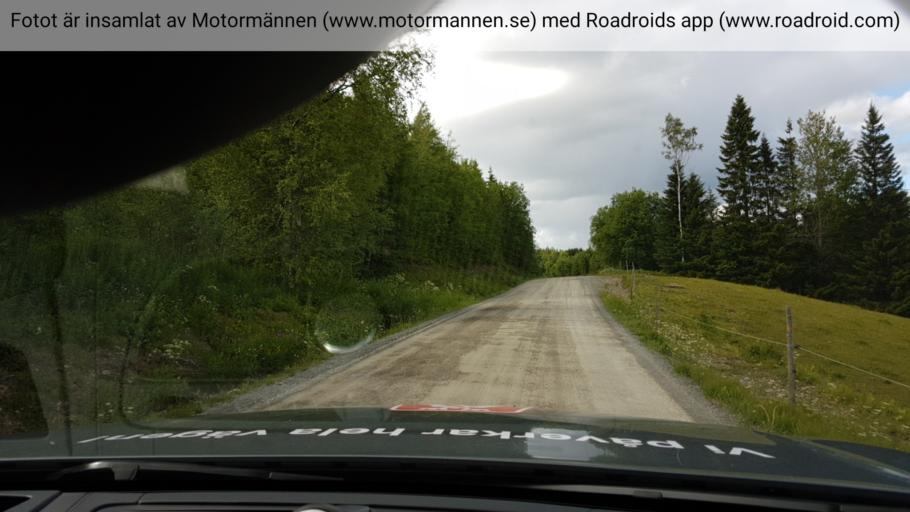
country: SE
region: Jaemtland
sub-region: Bergs Kommun
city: Hoverberg
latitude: 62.9257
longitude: 14.2982
